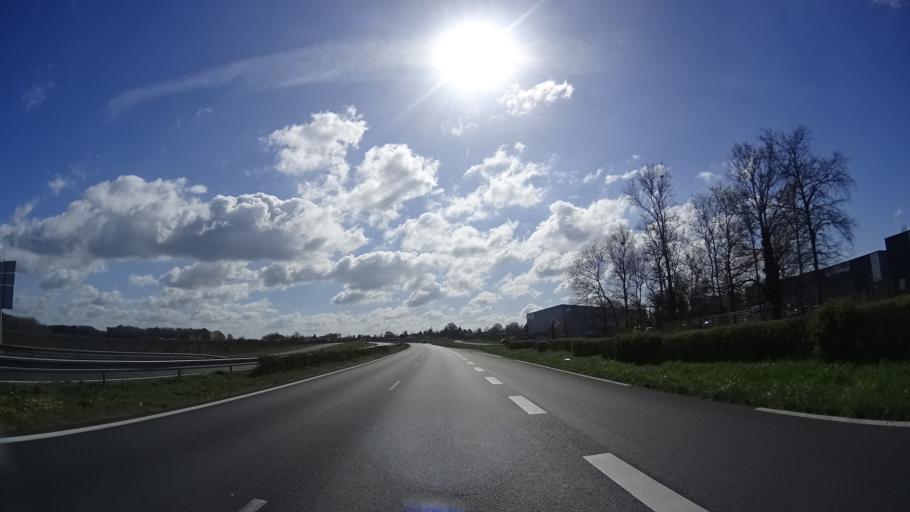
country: FR
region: Pays de la Loire
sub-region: Departement de Maine-et-Loire
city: Saint-Melaine-sur-Aubance
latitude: 47.3910
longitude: -0.5008
